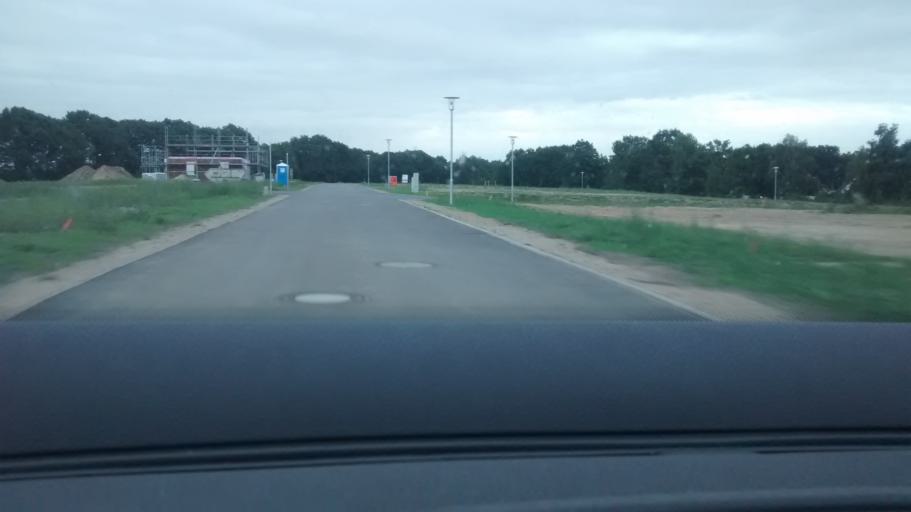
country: DE
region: Mecklenburg-Vorpommern
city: Lubtheen
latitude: 53.3991
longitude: 10.9739
